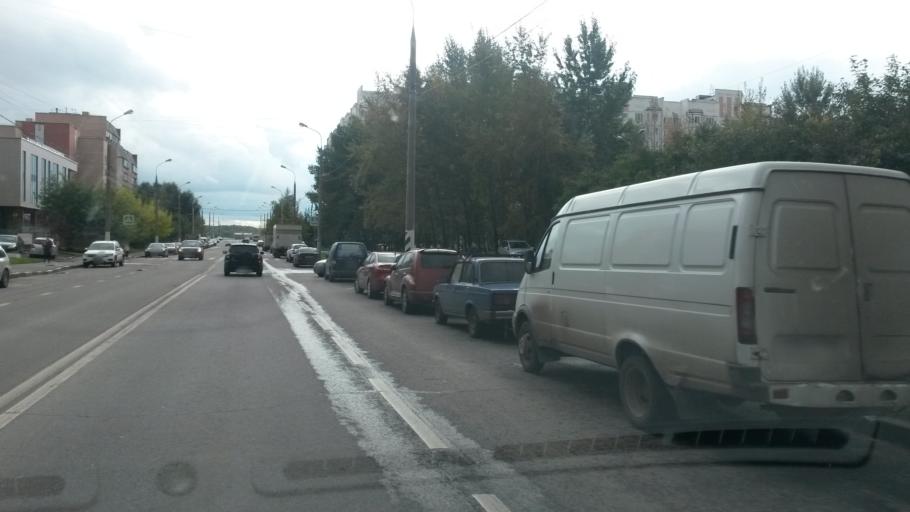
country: RU
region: Moskovskaya
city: Kommunarka
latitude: 55.5322
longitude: 37.5180
